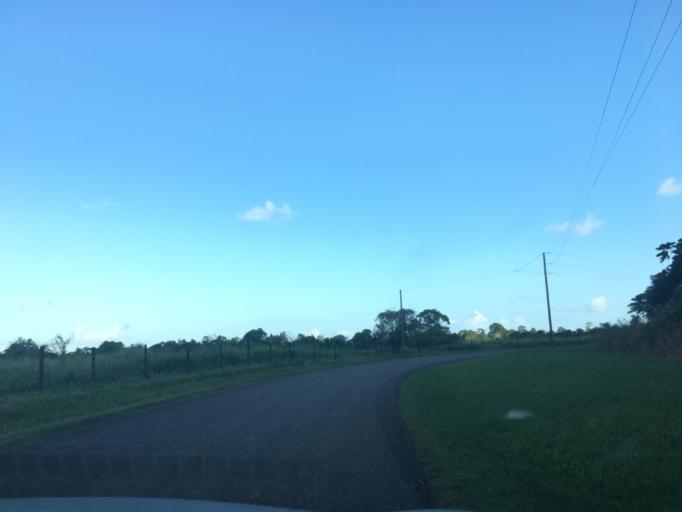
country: BZ
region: Stann Creek
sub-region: Dangriga
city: Dangriga
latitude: 16.8277
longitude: -88.3454
